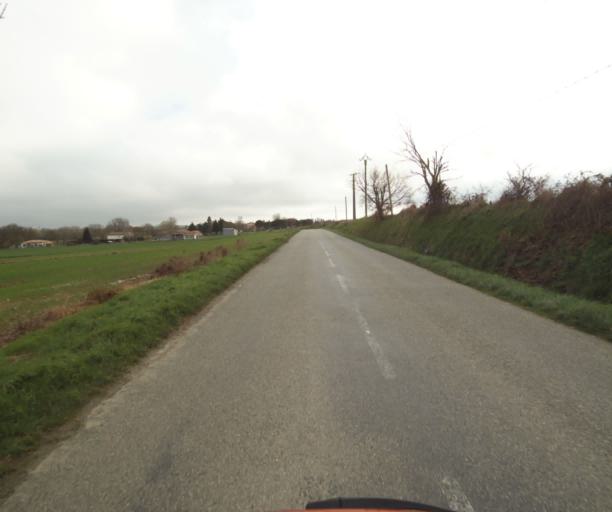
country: FR
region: Languedoc-Roussillon
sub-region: Departement de l'Aude
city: Belpech
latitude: 43.2046
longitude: 1.7318
